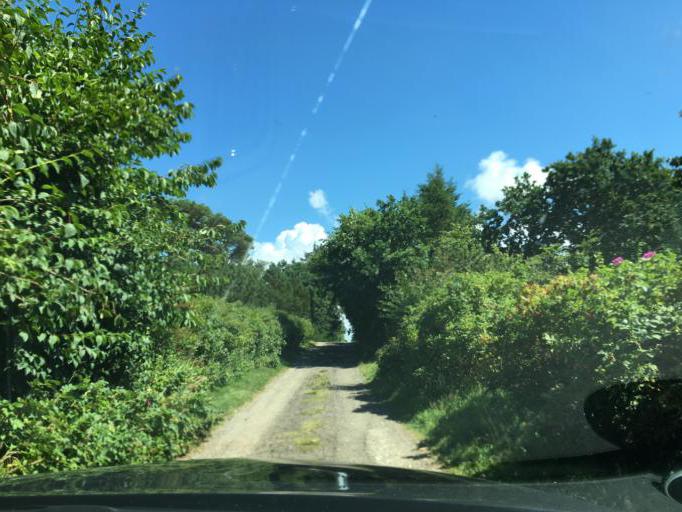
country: DK
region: Capital Region
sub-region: Gribskov Kommune
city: Helsinge
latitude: 56.0953
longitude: 12.1646
